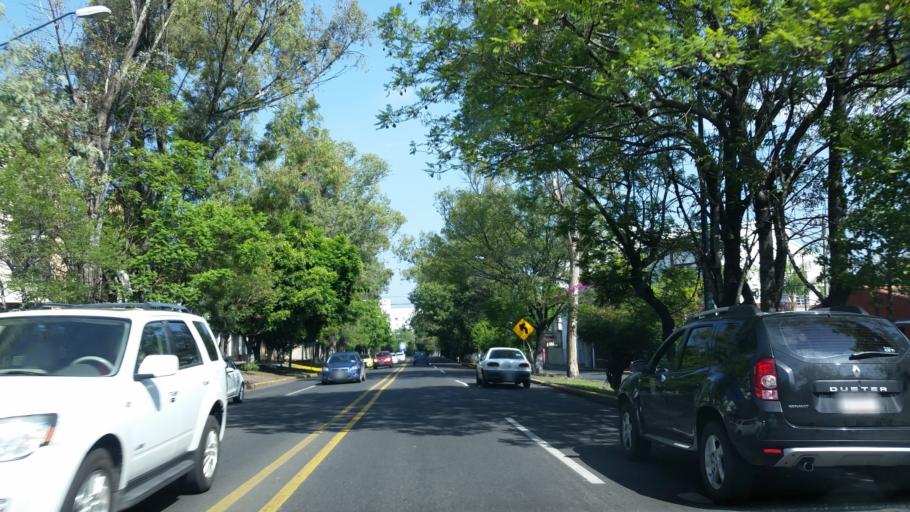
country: MX
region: Michoacan
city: Morelia
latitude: 19.6814
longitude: -101.1879
